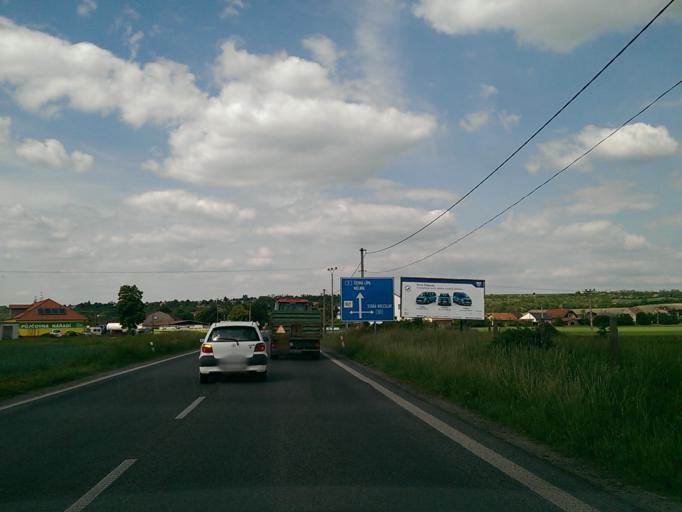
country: CZ
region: Central Bohemia
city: Libis
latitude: 50.3062
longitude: 14.5143
